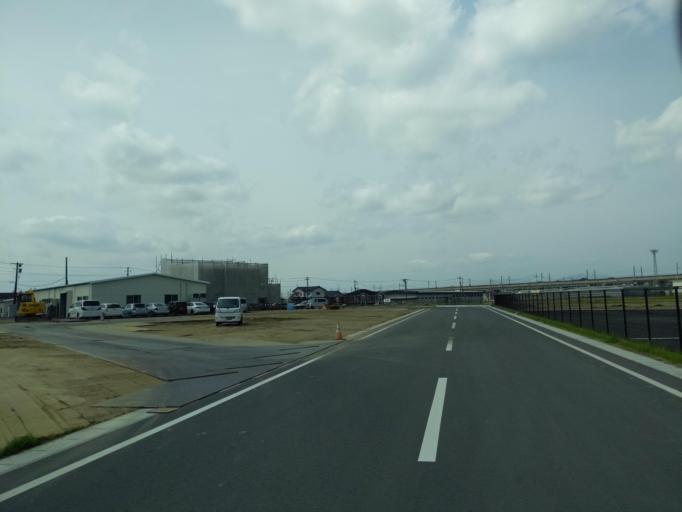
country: JP
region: Fukushima
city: Koriyama
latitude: 37.4240
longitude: 140.4015
